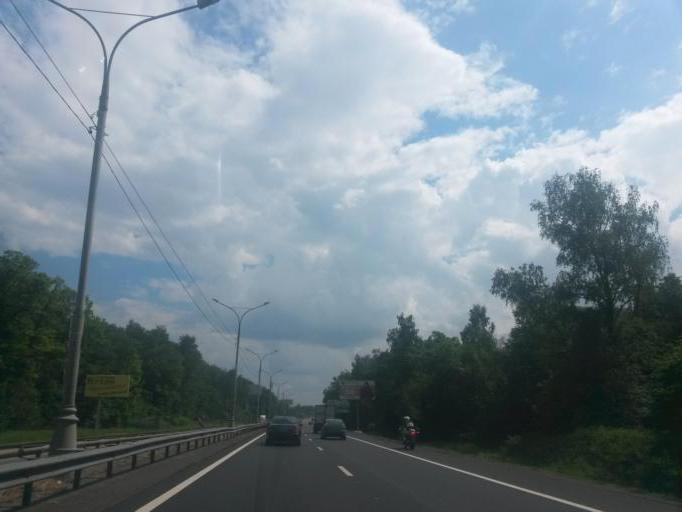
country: RU
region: Moskovskaya
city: Petrovskaya
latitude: 55.5393
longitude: 37.8055
